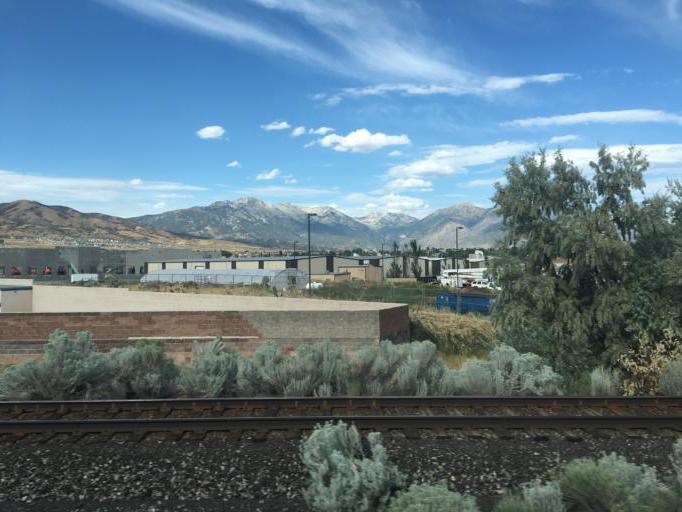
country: US
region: Utah
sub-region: Utah County
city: Lehi
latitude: 40.4096
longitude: -111.8785
